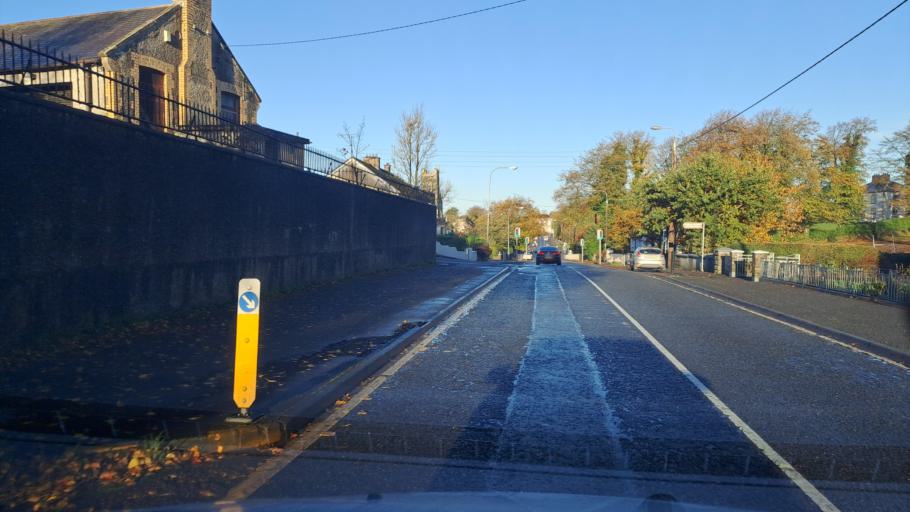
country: IE
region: Ulster
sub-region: An Cabhan
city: Cootehill
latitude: 54.0731
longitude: -7.0742
